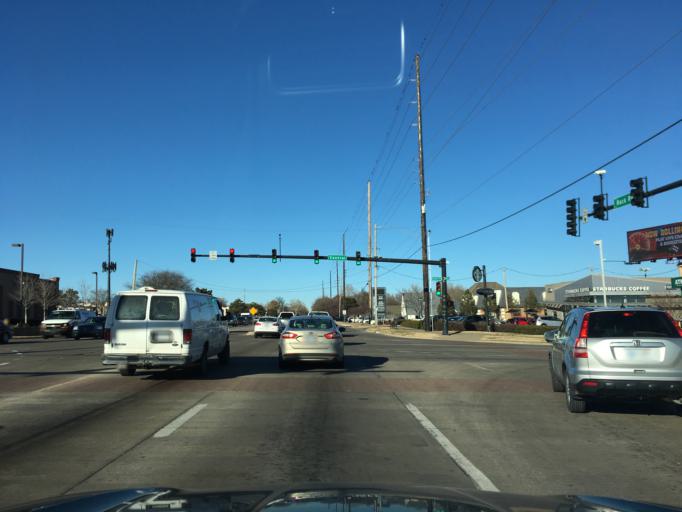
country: US
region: Kansas
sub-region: Sedgwick County
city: Bellaire
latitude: 37.6935
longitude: -97.2445
